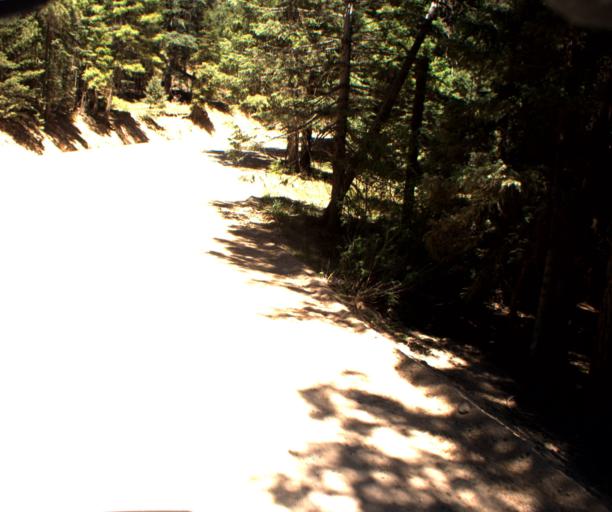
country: US
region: Arizona
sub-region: Graham County
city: Swift Trail Junction
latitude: 32.6709
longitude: -109.8830
